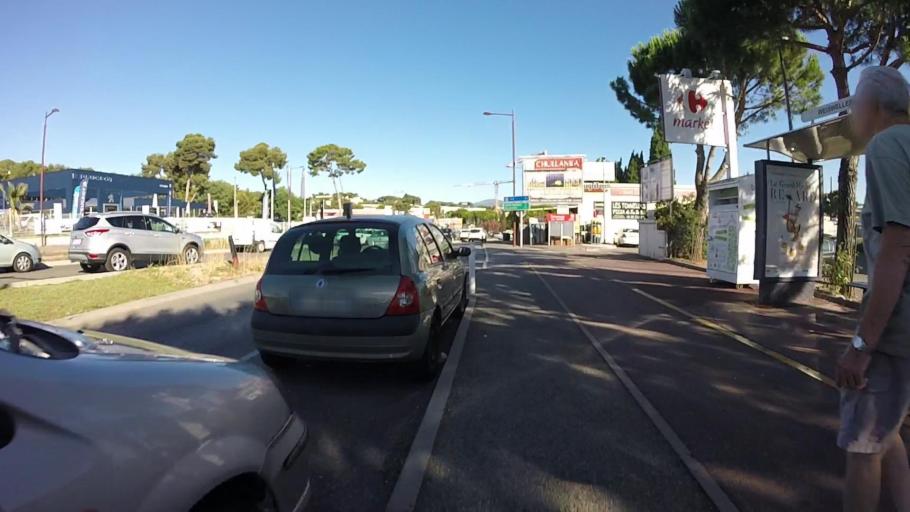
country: FR
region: Provence-Alpes-Cote d'Azur
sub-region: Departement des Alpes-Maritimes
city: Biot
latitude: 43.5980
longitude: 7.0885
